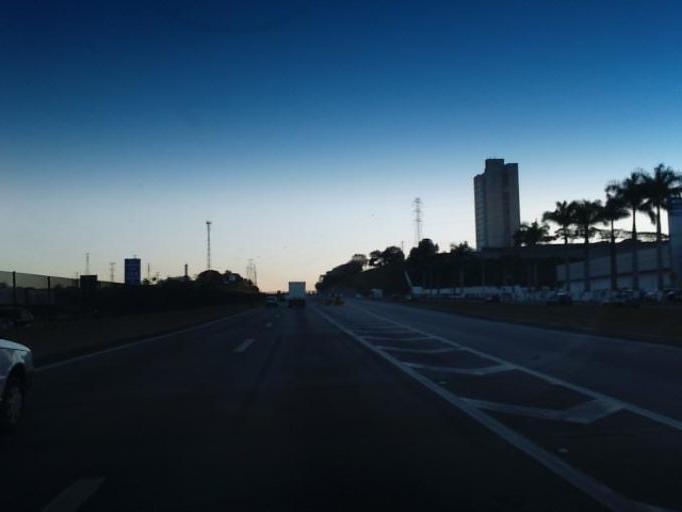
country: BR
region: Sao Paulo
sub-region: Sao Jose Dos Campos
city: Sao Jose dos Campos
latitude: -23.1813
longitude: -45.8438
